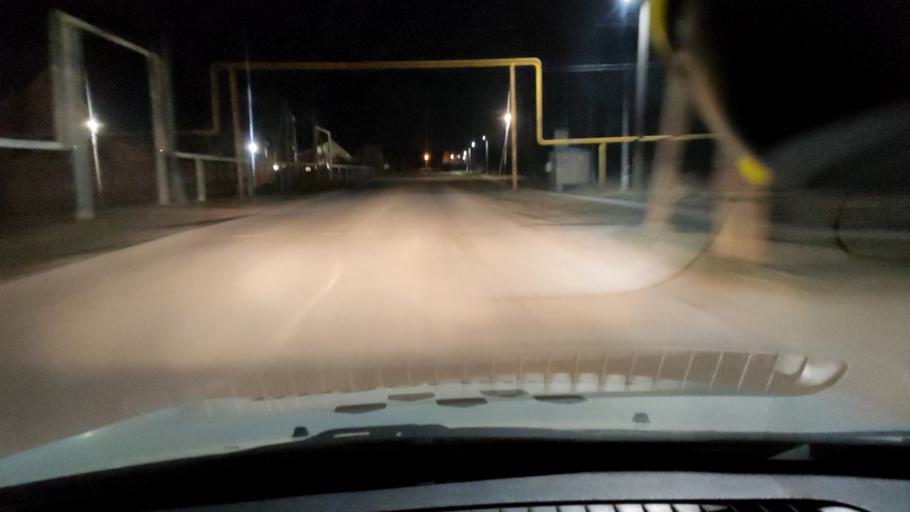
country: RU
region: Samara
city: Podstepki
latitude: 53.6217
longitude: 49.0470
